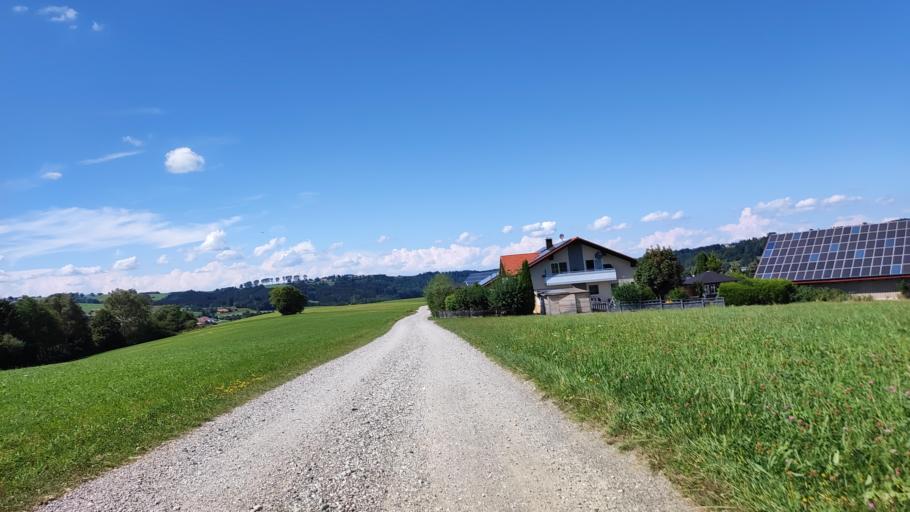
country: DE
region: Bavaria
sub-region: Swabia
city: Obergunzburg
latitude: 47.8415
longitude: 10.4291
